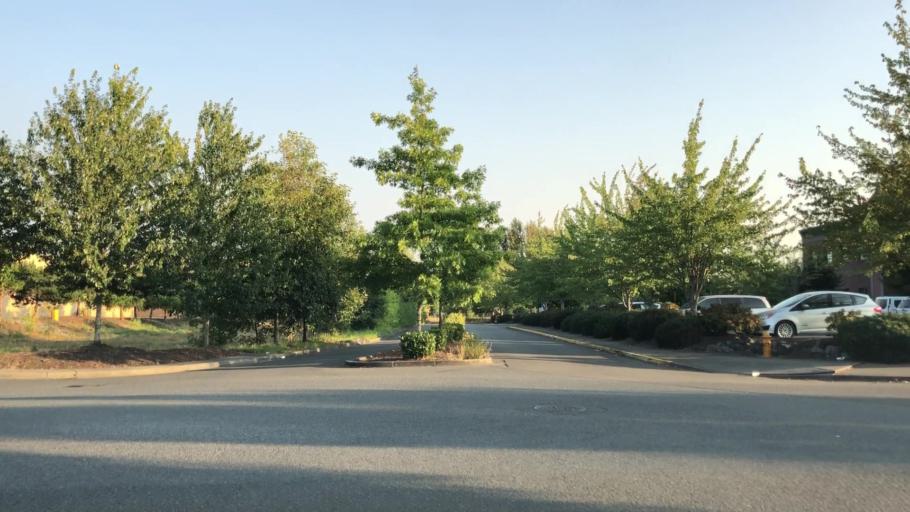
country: US
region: Washington
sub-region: Snohomish County
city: Smokey Point
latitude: 48.1518
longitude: -122.1766
